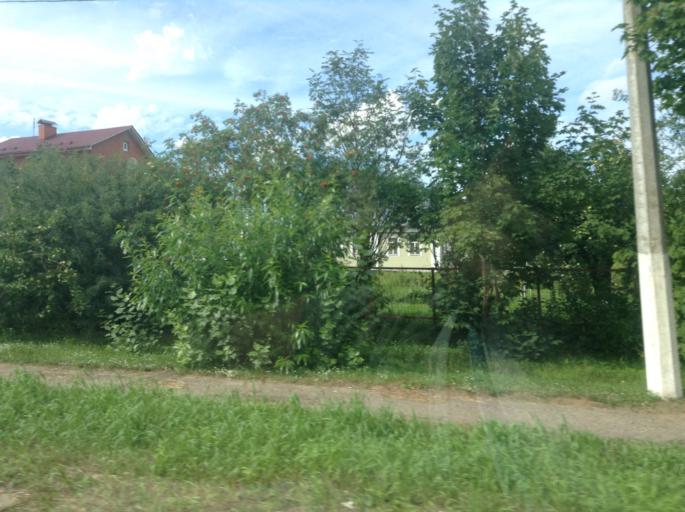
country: RU
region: Moskovskaya
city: Yegor'yevsk
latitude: 55.3622
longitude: 39.0975
